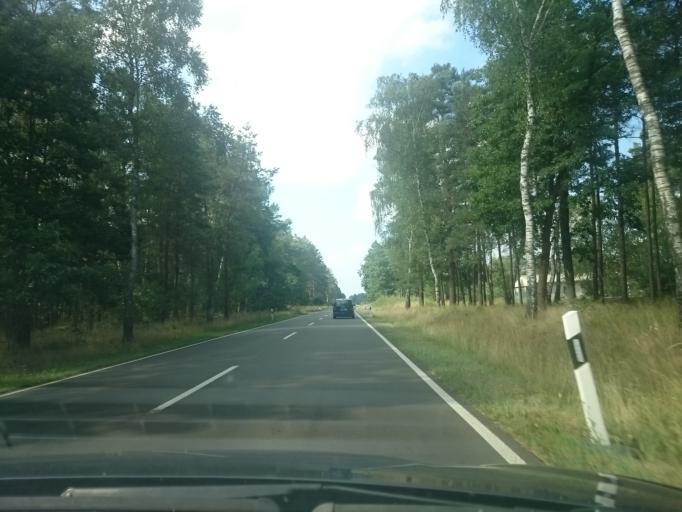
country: DE
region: Mecklenburg-Vorpommern
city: Torgelow
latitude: 53.6038
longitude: 14.0479
